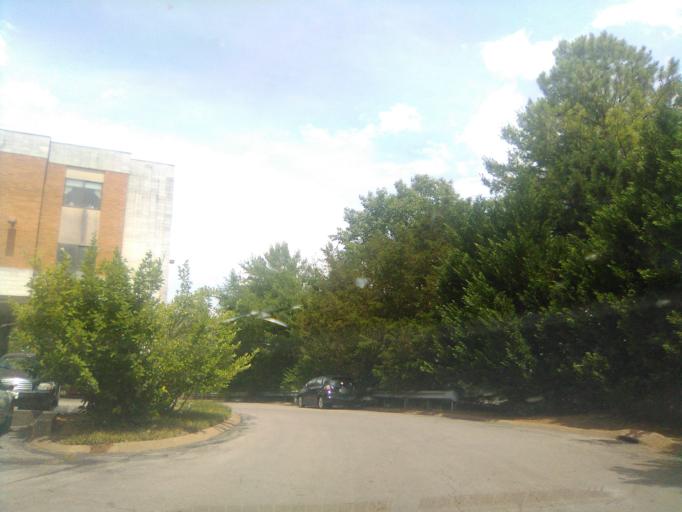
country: US
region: Tennessee
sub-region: Davidson County
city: Belle Meade
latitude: 36.0891
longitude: -86.8887
